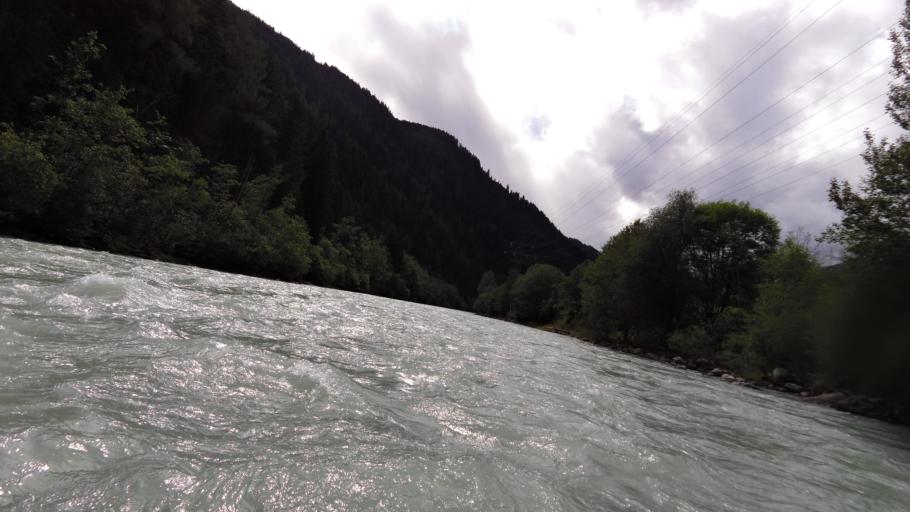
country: AT
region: Tyrol
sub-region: Politischer Bezirk Landeck
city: Landeck
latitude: 47.1243
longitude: 10.5873
